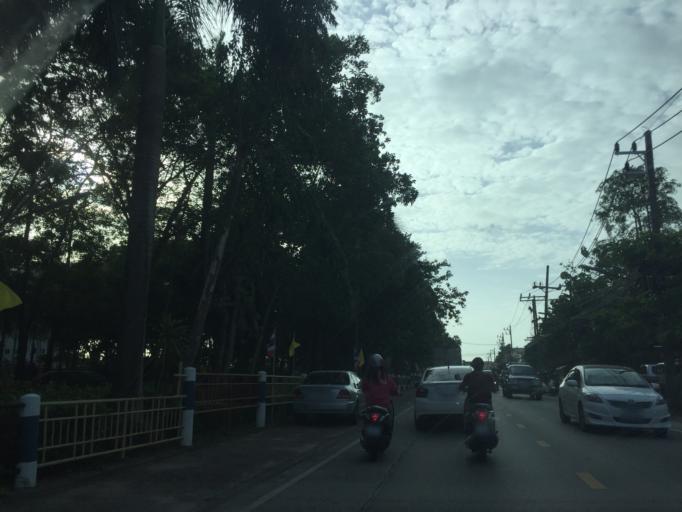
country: TH
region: Phuket
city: Mueang Phuket
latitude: 7.8618
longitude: 98.3722
